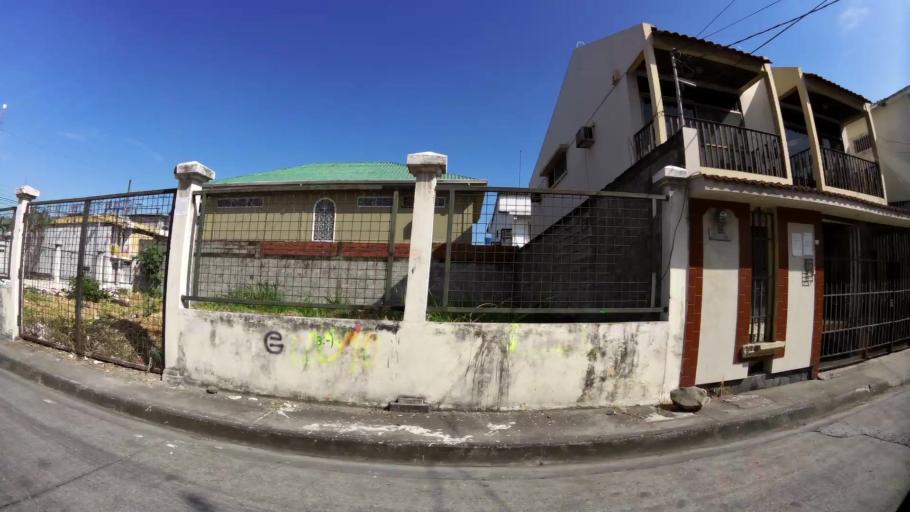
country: EC
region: Guayas
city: Guayaquil
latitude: -2.2295
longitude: -79.8911
